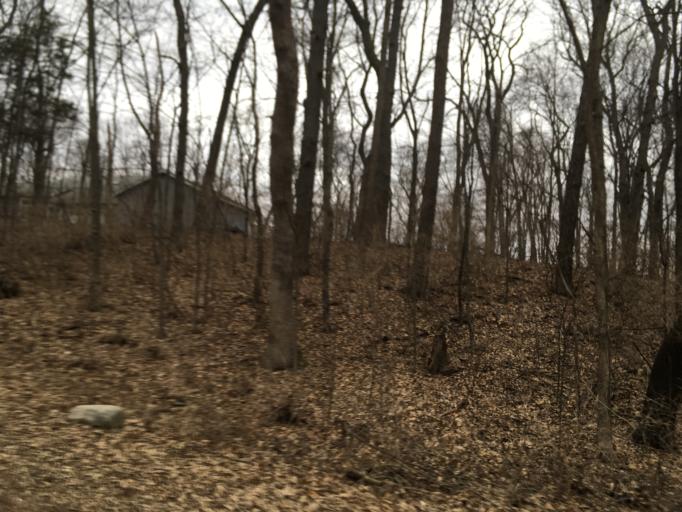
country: US
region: Michigan
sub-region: Washtenaw County
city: Chelsea
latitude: 42.3555
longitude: -84.1164
